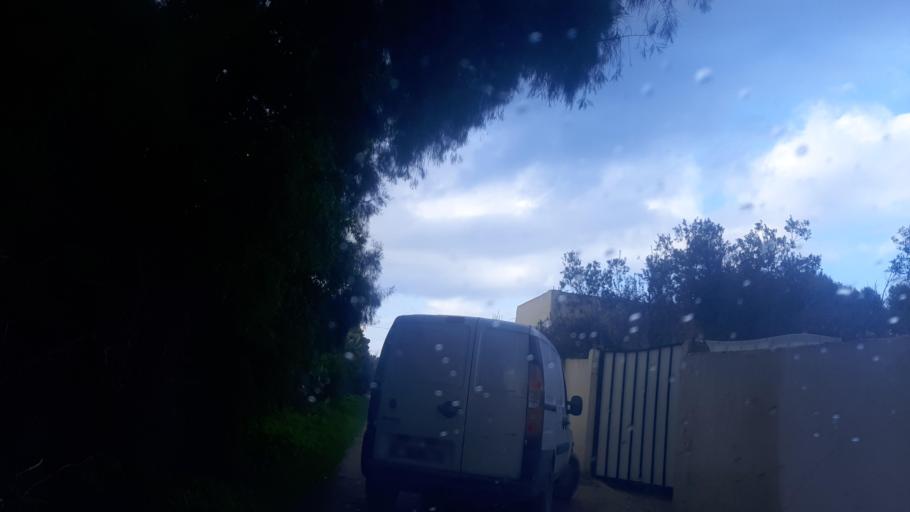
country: TN
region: Nabul
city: Manzil Bu Zalafah
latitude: 36.7405
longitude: 10.5294
